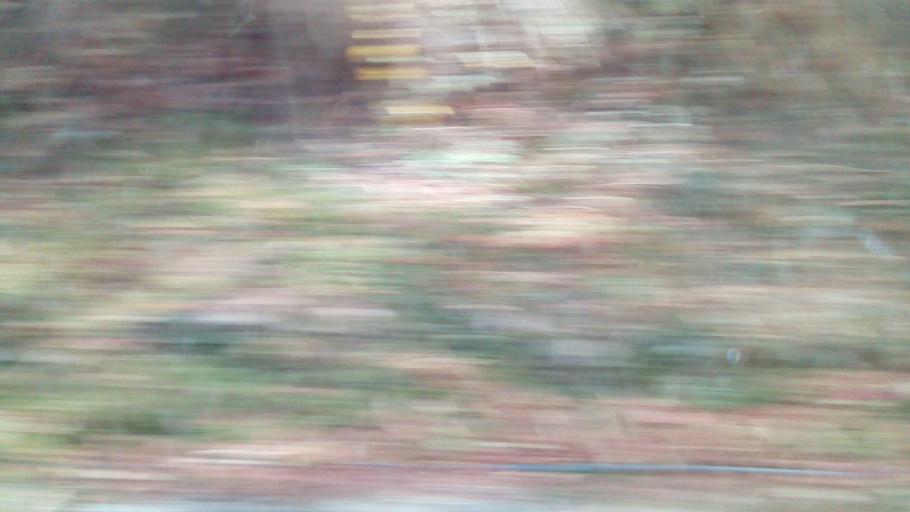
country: TW
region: Taiwan
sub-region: Hualien
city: Hualian
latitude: 24.3704
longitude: 121.3399
